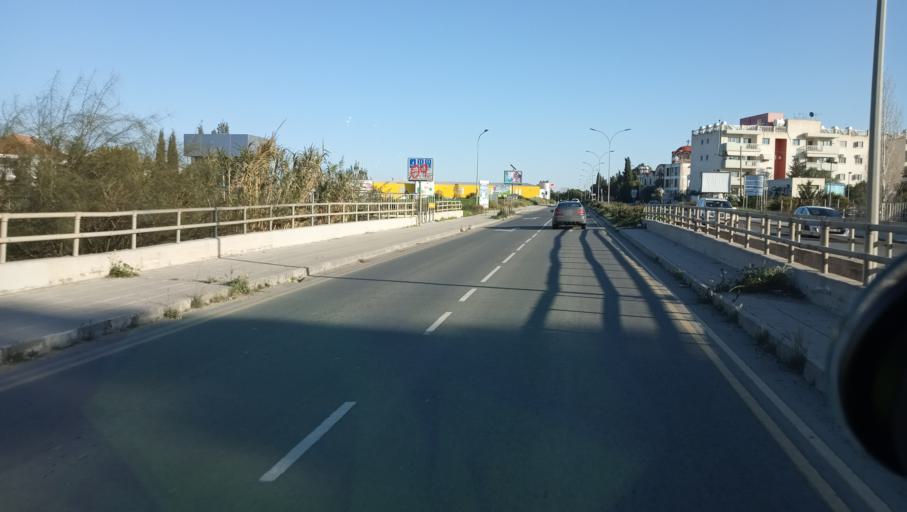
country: CY
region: Lefkosia
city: Tseri
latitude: 35.1306
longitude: 33.3155
